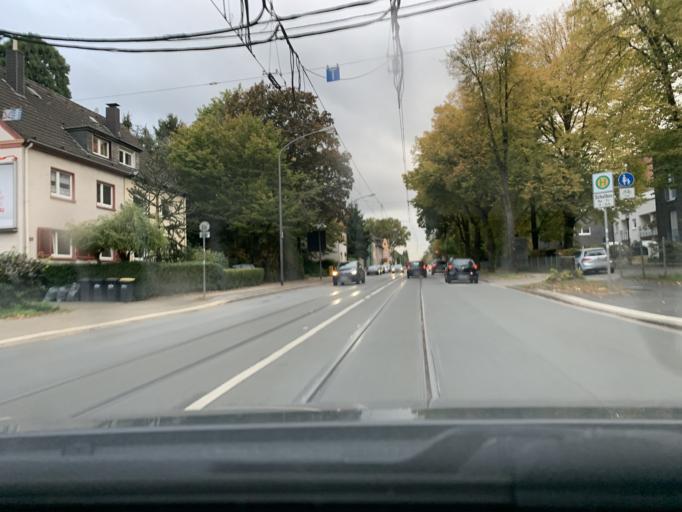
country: DE
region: North Rhine-Westphalia
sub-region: Regierungsbezirk Dusseldorf
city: Oberhausen
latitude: 51.4636
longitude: 6.9313
